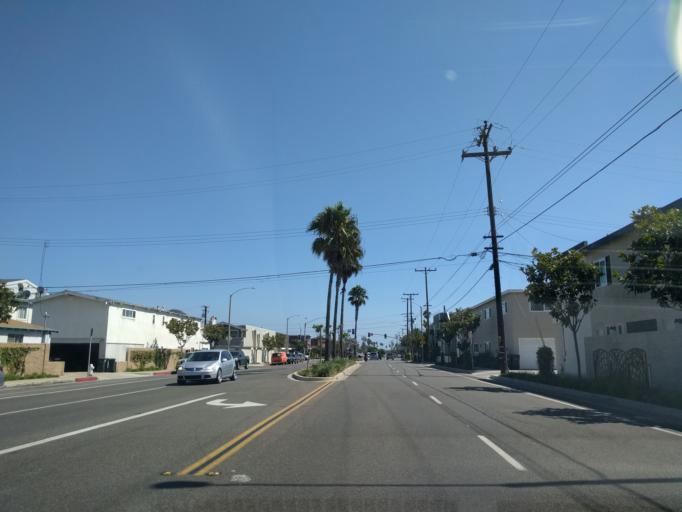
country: US
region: California
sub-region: Orange County
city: Newport Beach
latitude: 33.6158
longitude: -117.9336
